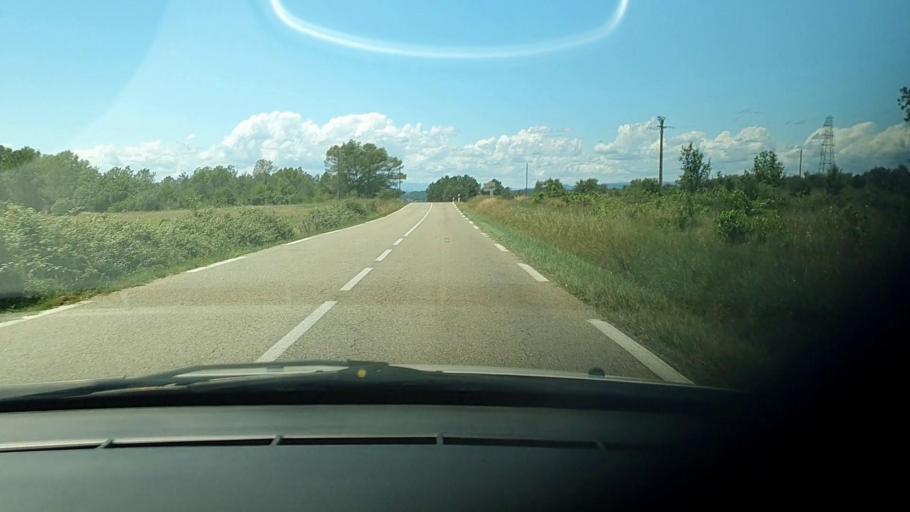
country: FR
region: Languedoc-Roussillon
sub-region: Departement du Gard
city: Moussac
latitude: 44.0657
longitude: 4.2464
